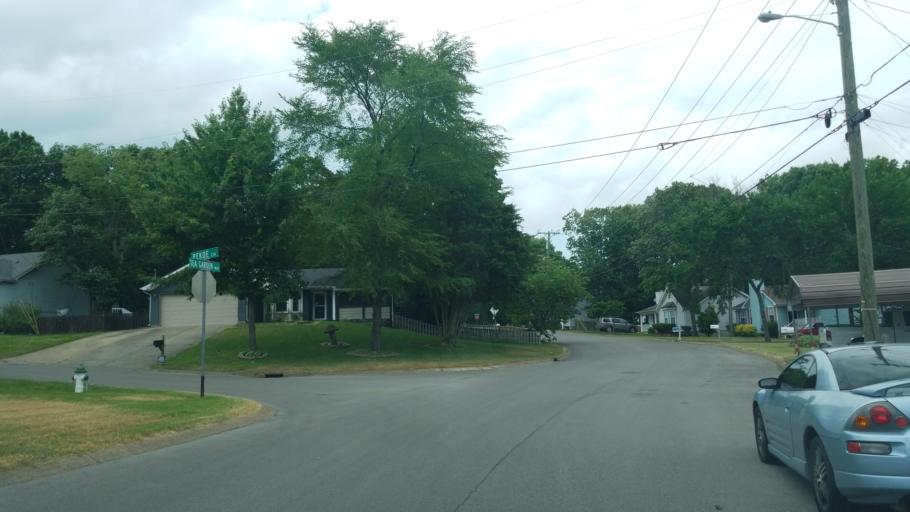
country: US
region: Tennessee
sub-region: Rutherford County
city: La Vergne
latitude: 36.0673
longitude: -86.6119
